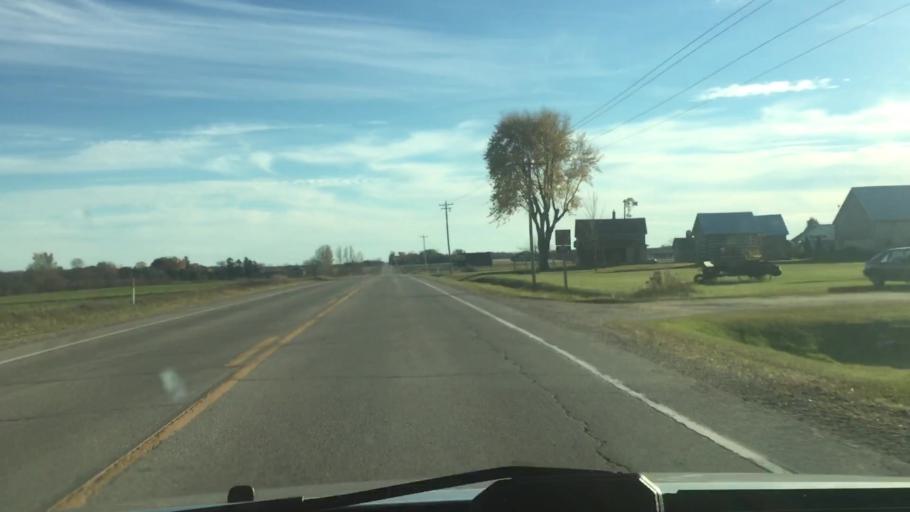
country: US
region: Wisconsin
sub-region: Kewaunee County
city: Kewaunee
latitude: 44.4063
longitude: -87.5422
